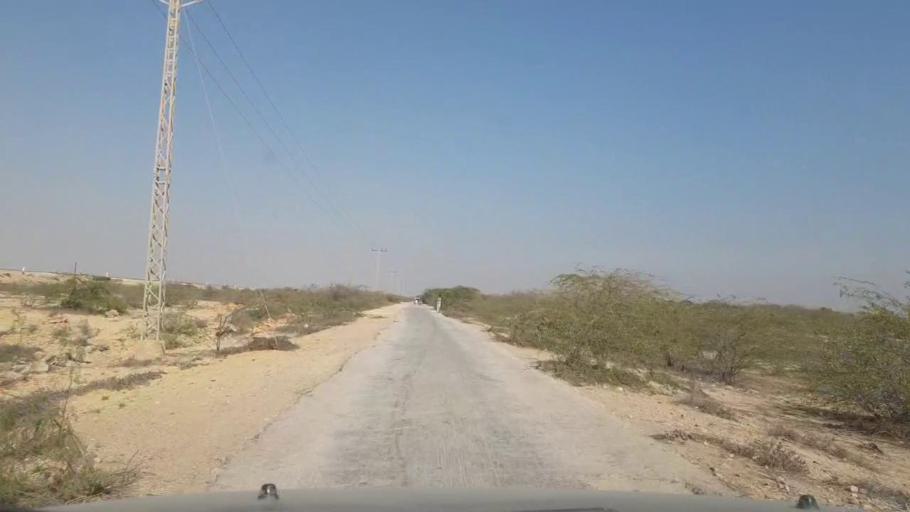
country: PK
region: Sindh
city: Daro Mehar
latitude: 24.9973
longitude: 68.0106
